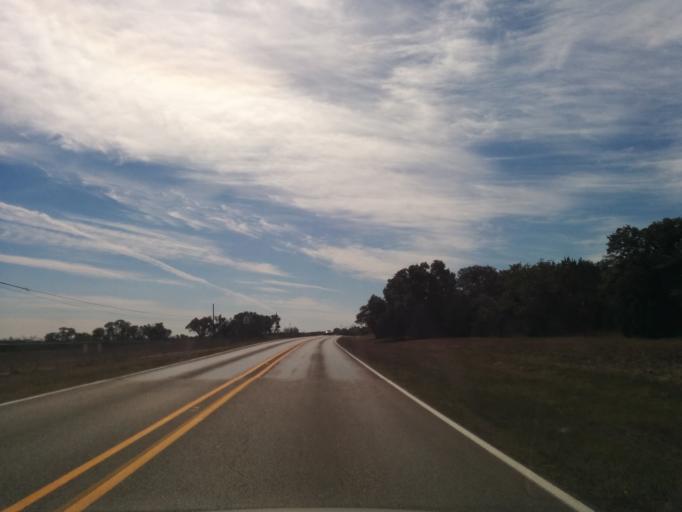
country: US
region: Texas
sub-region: Bexar County
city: Fair Oaks Ranch
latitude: 29.7249
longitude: -98.6235
